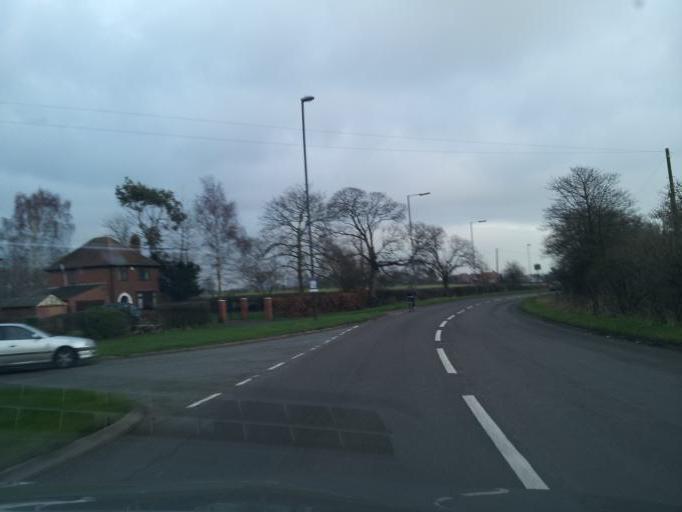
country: GB
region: England
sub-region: Derbyshire
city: Repton
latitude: 52.8535
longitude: -1.5803
